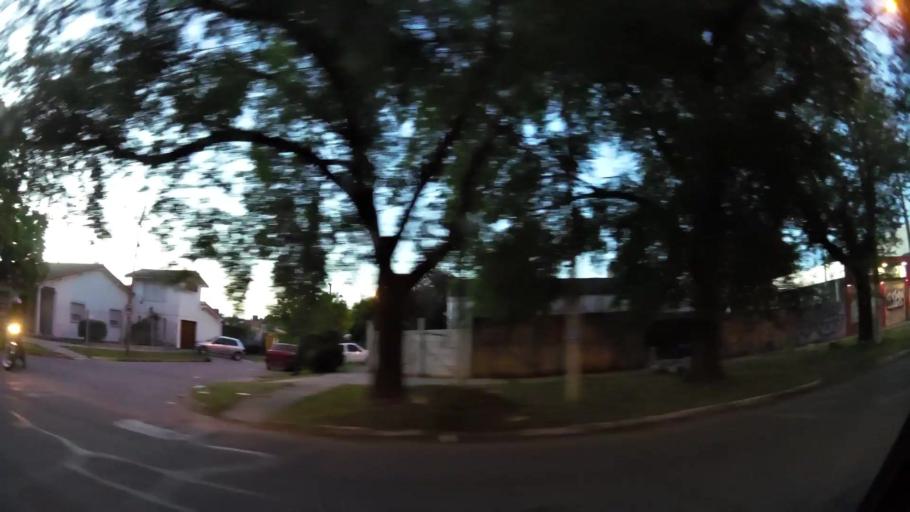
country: AR
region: Buenos Aires
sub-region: Partido de Quilmes
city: Quilmes
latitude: -34.7755
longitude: -58.2177
